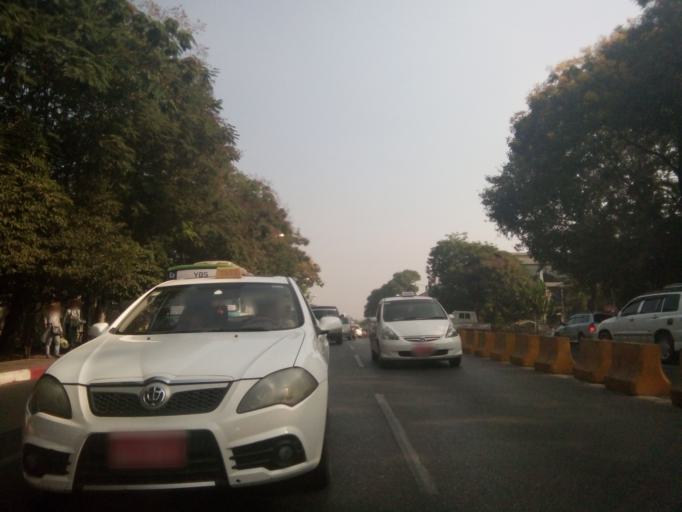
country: MM
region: Yangon
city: Yangon
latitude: 16.8556
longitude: 96.1411
